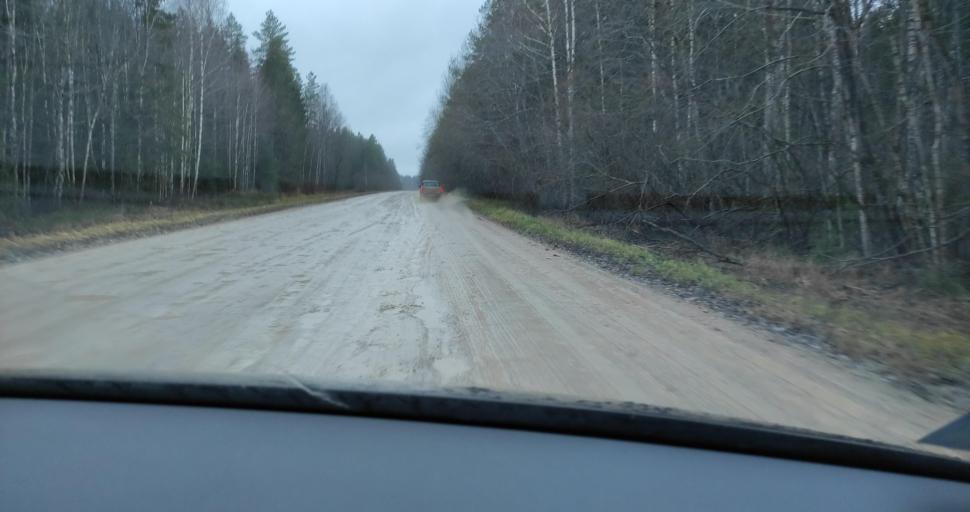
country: LV
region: Skrunda
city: Skrunda
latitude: 56.5843
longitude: 22.1279
